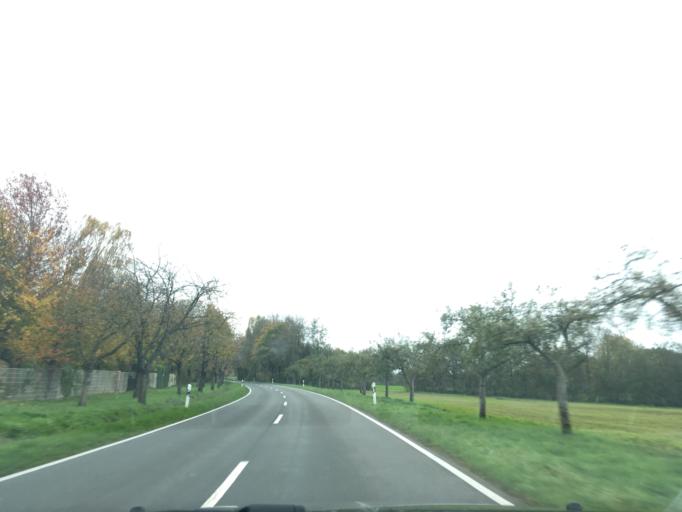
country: DE
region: North Rhine-Westphalia
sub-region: Regierungsbezirk Munster
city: Vreden
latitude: 52.0619
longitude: 6.7645
